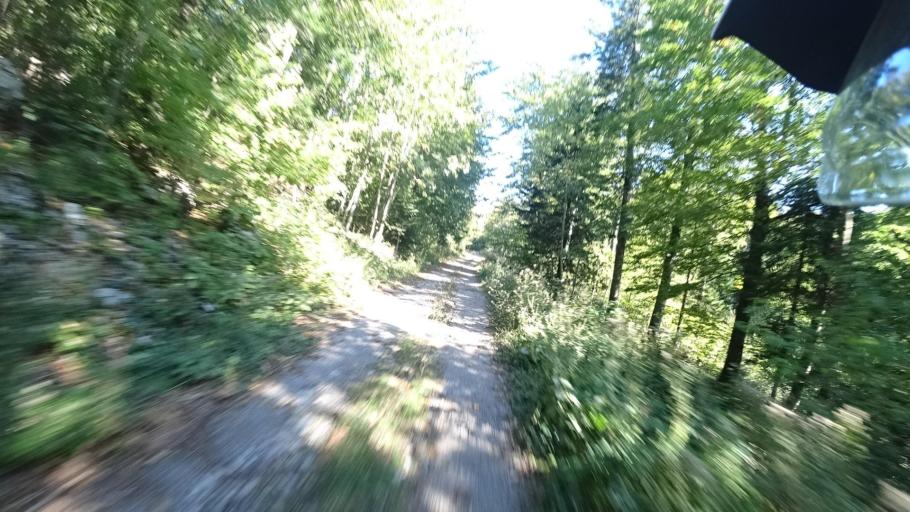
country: HR
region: Primorsko-Goranska
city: Vrbovsko
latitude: 45.2860
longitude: 15.1231
